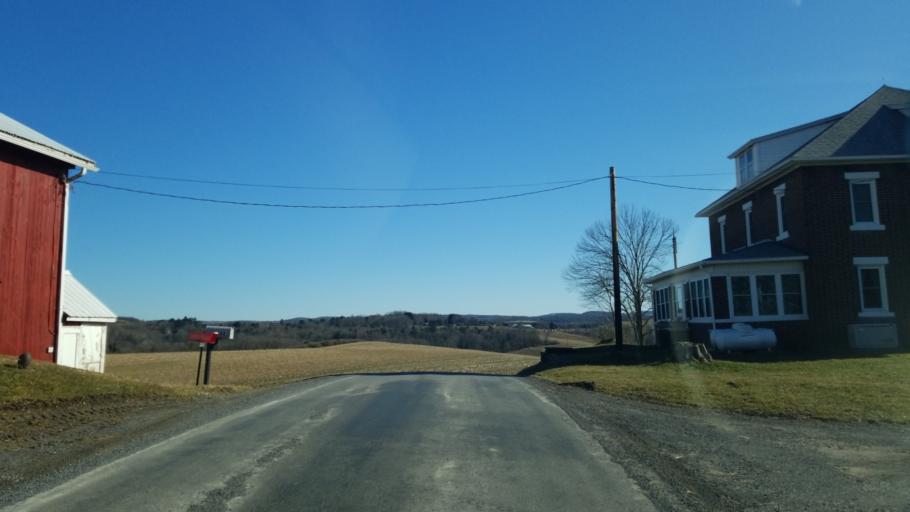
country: US
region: Pennsylvania
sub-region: Jefferson County
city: Sykesville
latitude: 41.0423
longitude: -78.7836
